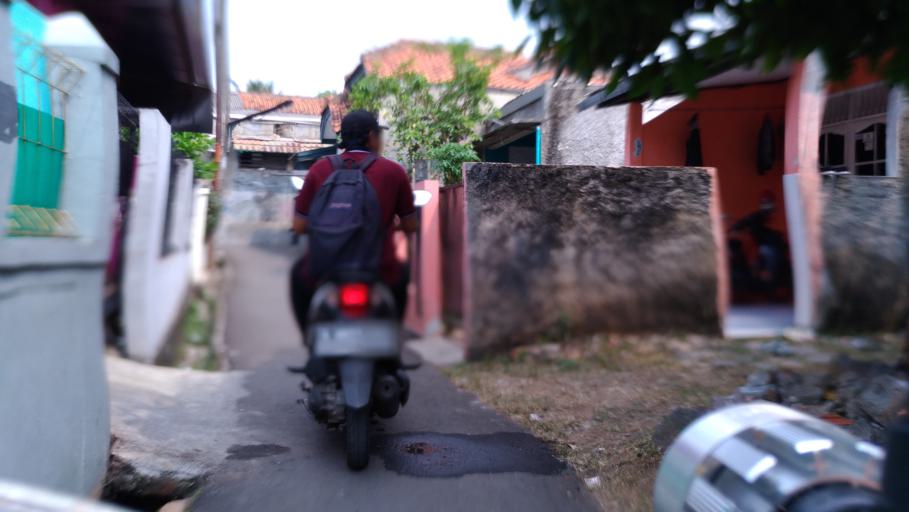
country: ID
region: West Java
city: Depok
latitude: -6.3571
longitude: 106.8760
